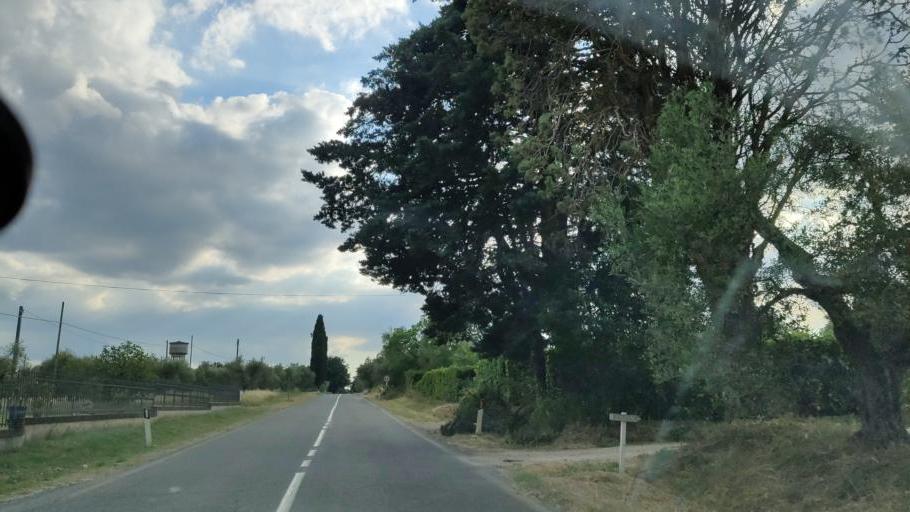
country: IT
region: Umbria
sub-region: Provincia di Terni
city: Penna in Teverina
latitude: 42.5137
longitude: 12.3525
